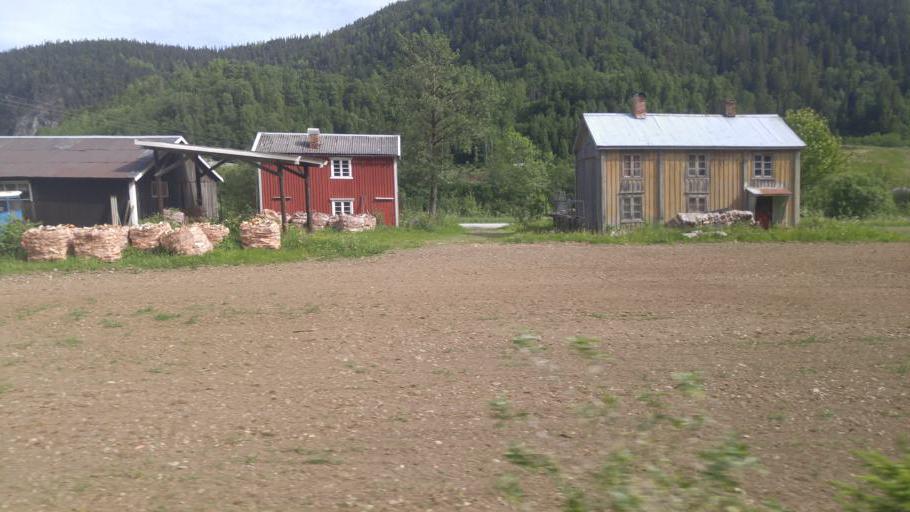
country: NO
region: Sor-Trondelag
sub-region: Midtre Gauldal
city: Storen
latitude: 63.0684
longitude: 10.2697
